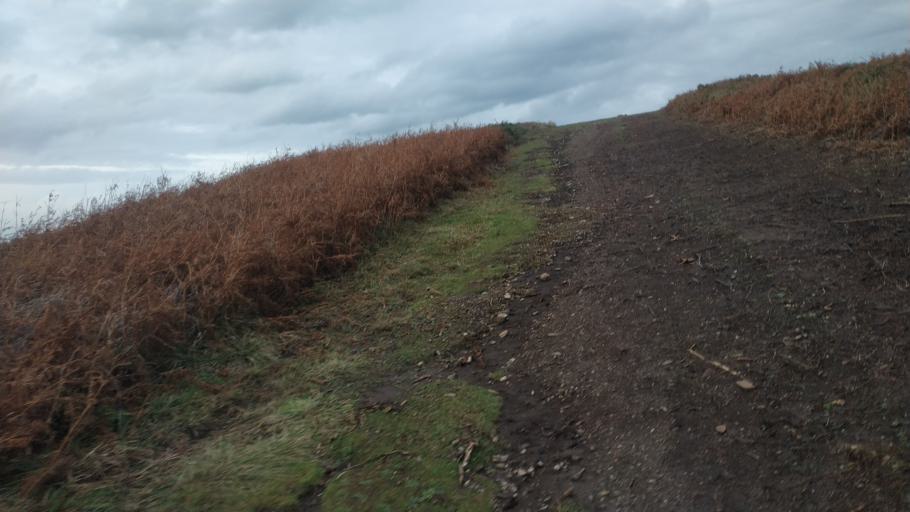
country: ES
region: Galicia
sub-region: Provincia da Coruna
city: Oleiros
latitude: 43.4021
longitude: -8.3288
